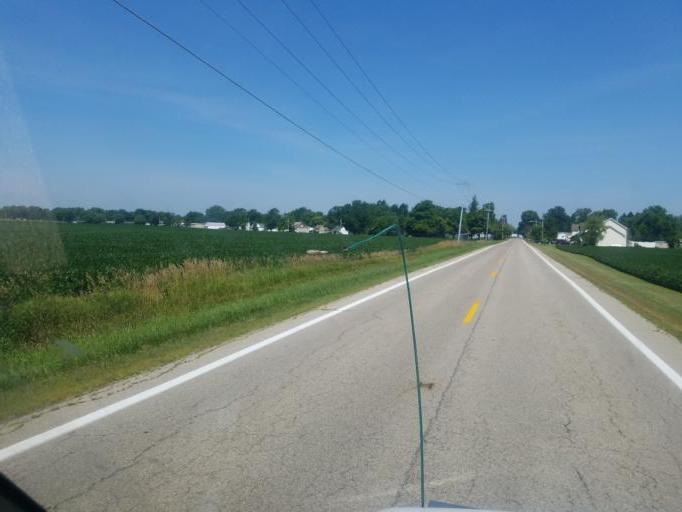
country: US
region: Ohio
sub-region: Champaign County
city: North Lewisburg
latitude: 40.2188
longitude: -83.5493
